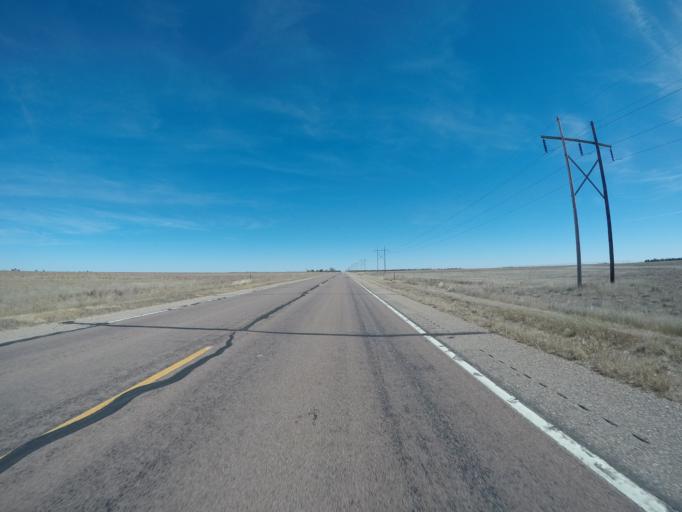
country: US
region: Colorado
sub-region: Yuma County
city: Yuma
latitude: 39.6552
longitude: -102.7775
